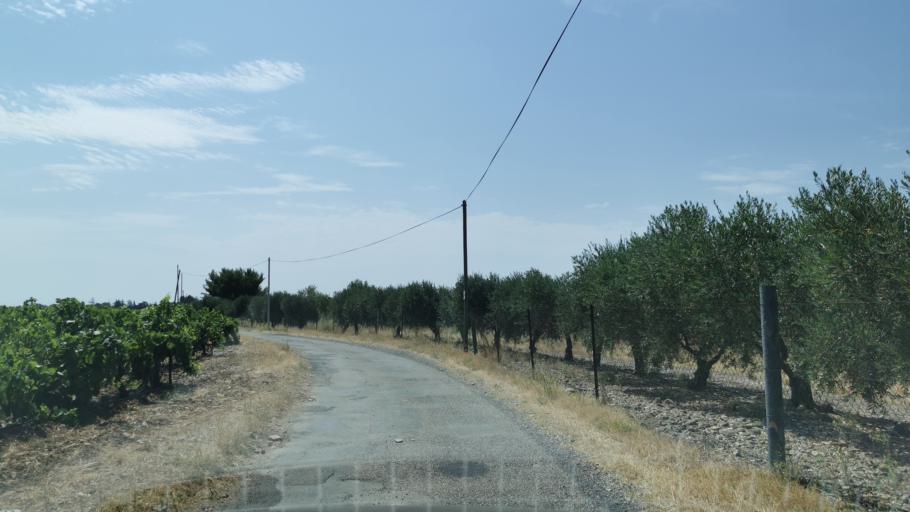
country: FR
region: Languedoc-Roussillon
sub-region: Departement de l'Aude
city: Bize-Minervois
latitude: 43.2988
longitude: 2.8757
